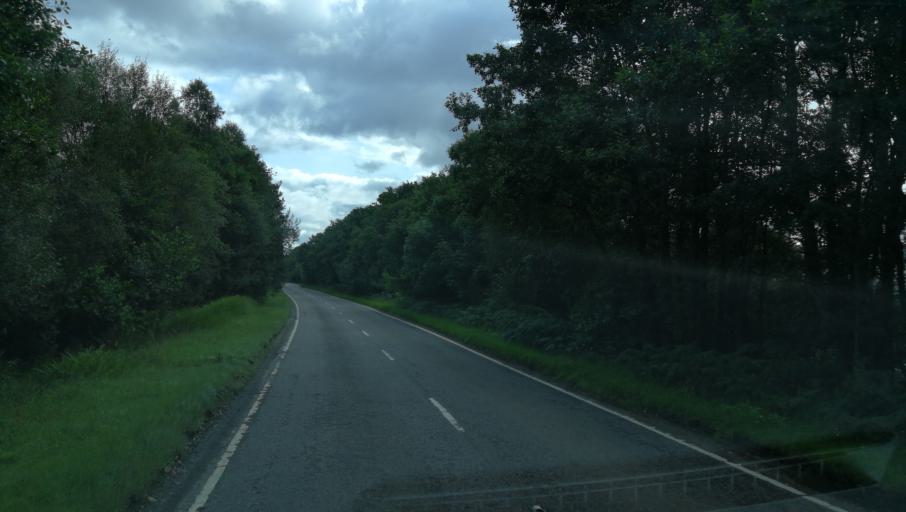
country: GB
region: Scotland
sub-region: Highland
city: Fort William
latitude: 56.8566
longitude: -5.3024
